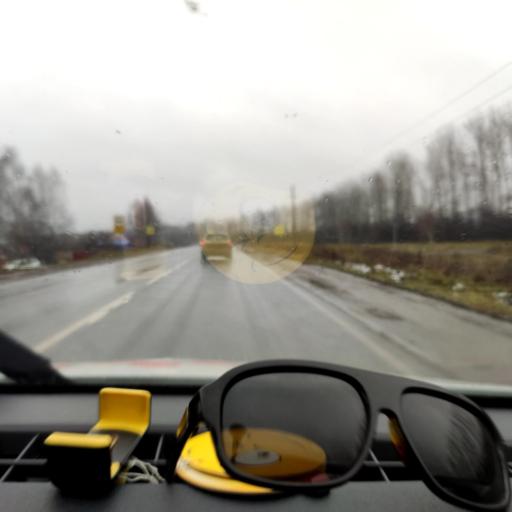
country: RU
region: Bashkortostan
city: Iglino
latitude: 54.7929
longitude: 56.2807
